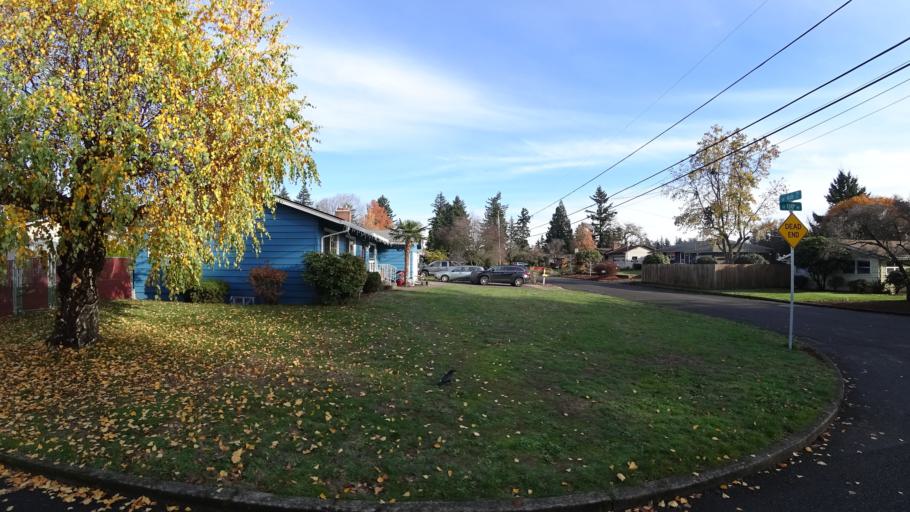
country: US
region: Oregon
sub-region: Multnomah County
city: Lents
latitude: 45.5212
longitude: -122.5295
